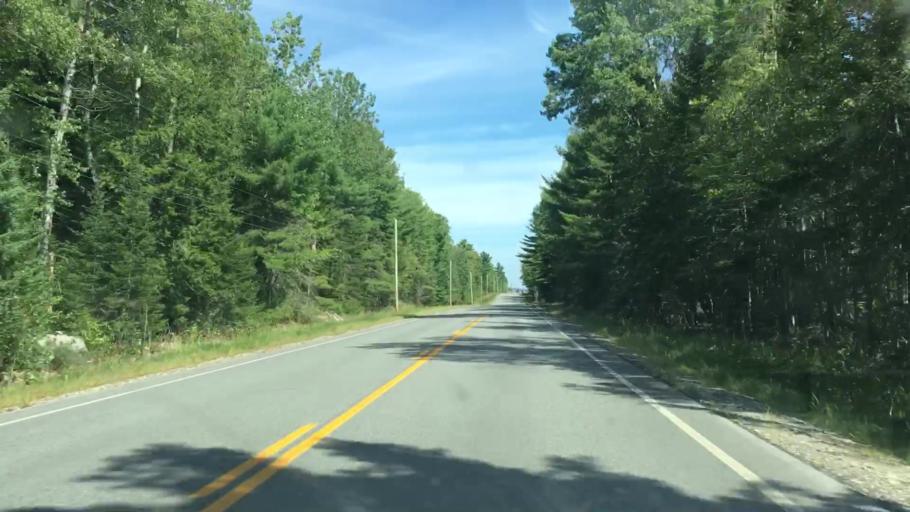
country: US
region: Maine
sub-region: Penobscot County
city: Howland
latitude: 45.2329
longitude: -68.6929
